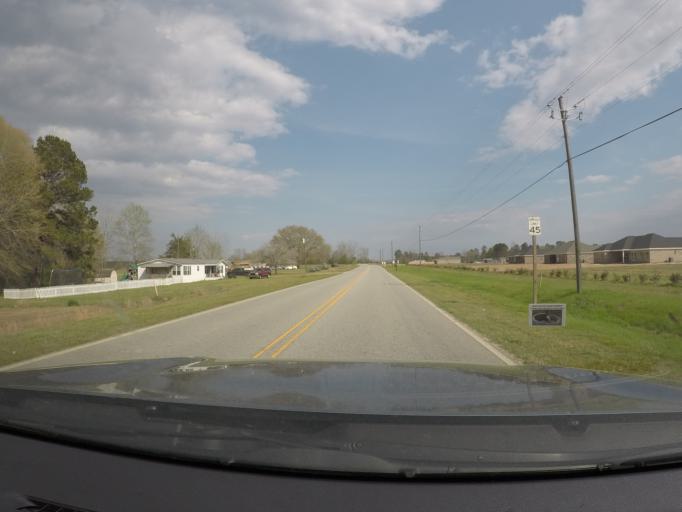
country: US
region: Georgia
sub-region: Bulloch County
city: Statesboro
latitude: 32.3594
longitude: -81.7695
